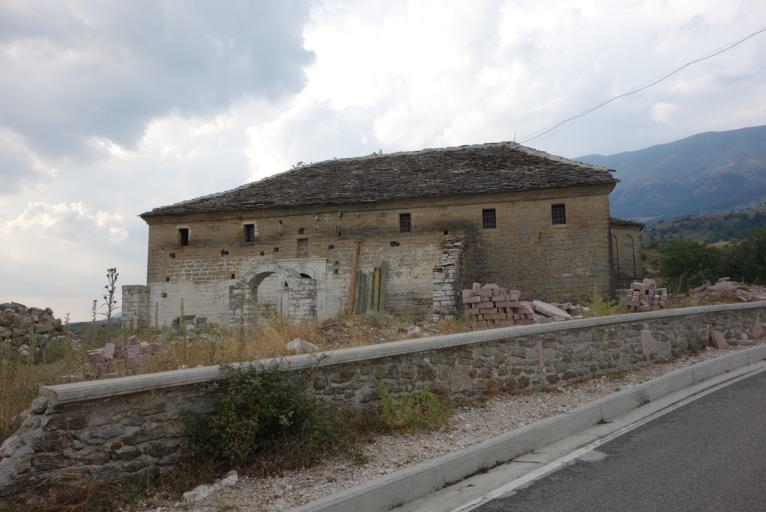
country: AL
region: Gjirokaster
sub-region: Rrethi i Gjirokastres
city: Qestorat
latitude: 40.1008
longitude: 20.2042
